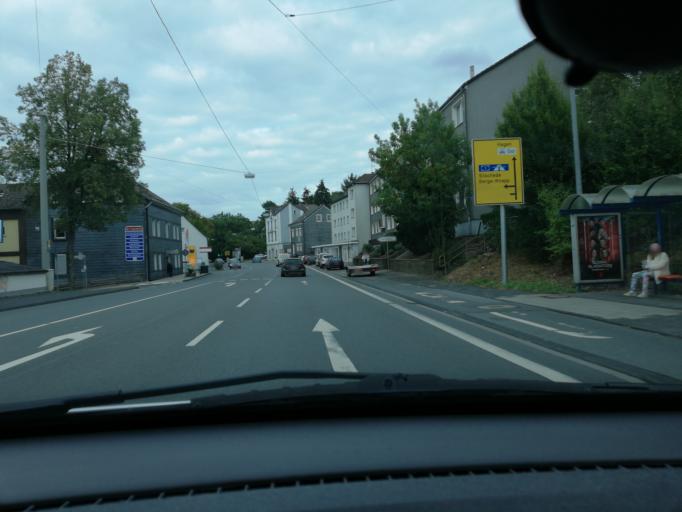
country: DE
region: North Rhine-Westphalia
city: Gevelsberg
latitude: 51.3291
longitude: 7.3674
